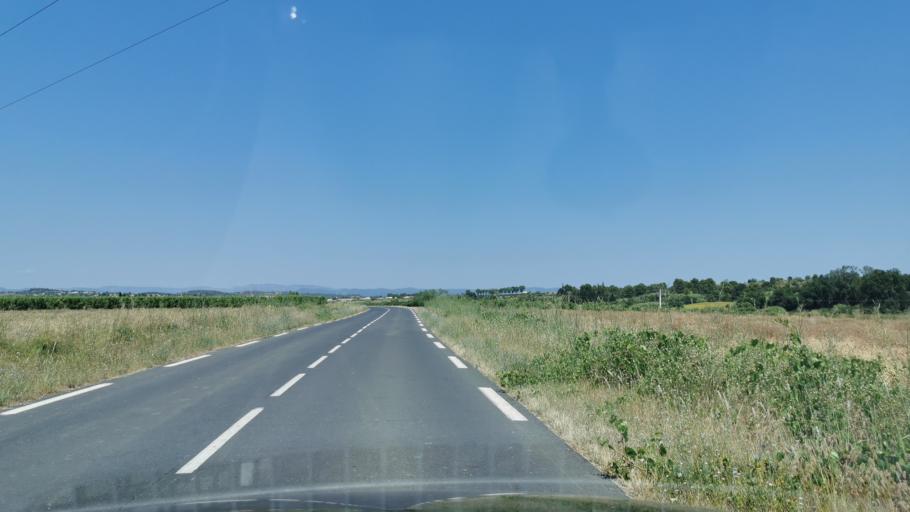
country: FR
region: Languedoc-Roussillon
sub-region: Departement de l'Herault
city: Maureilhan
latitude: 43.3722
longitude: 3.1133
